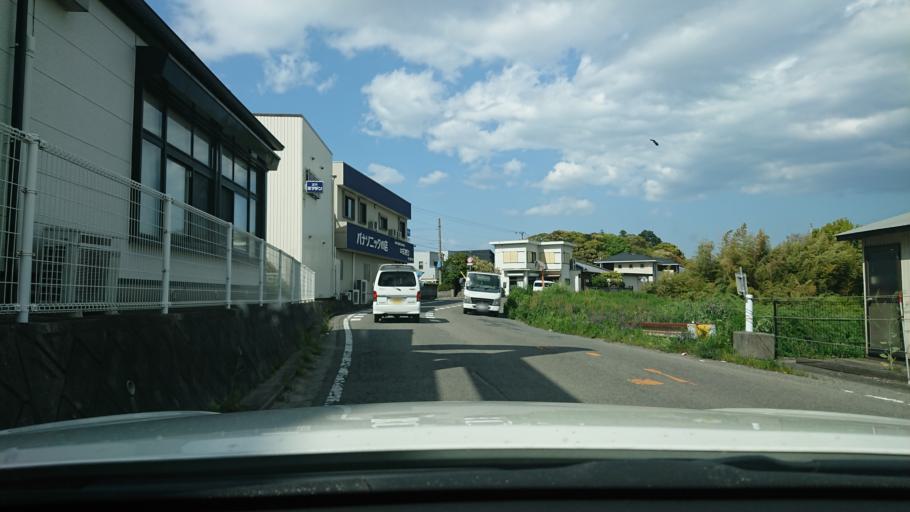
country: JP
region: Tokushima
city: Komatsushimacho
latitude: 34.0021
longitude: 134.5477
